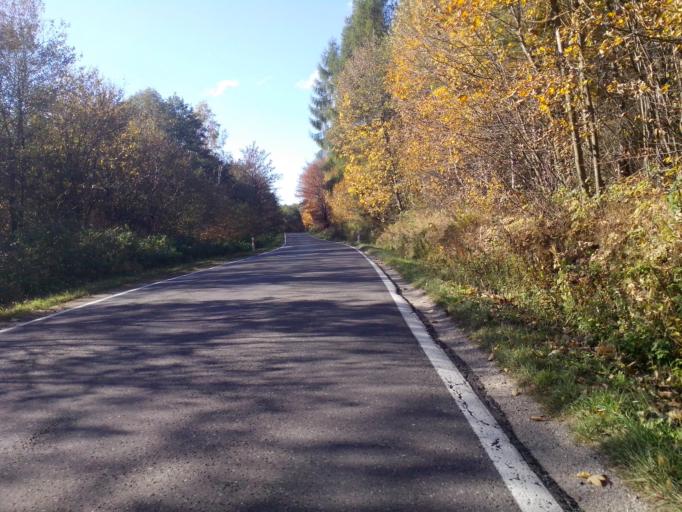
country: PL
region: Subcarpathian Voivodeship
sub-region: Powiat krosnienski
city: Korczyna
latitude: 49.7662
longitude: 21.8227
